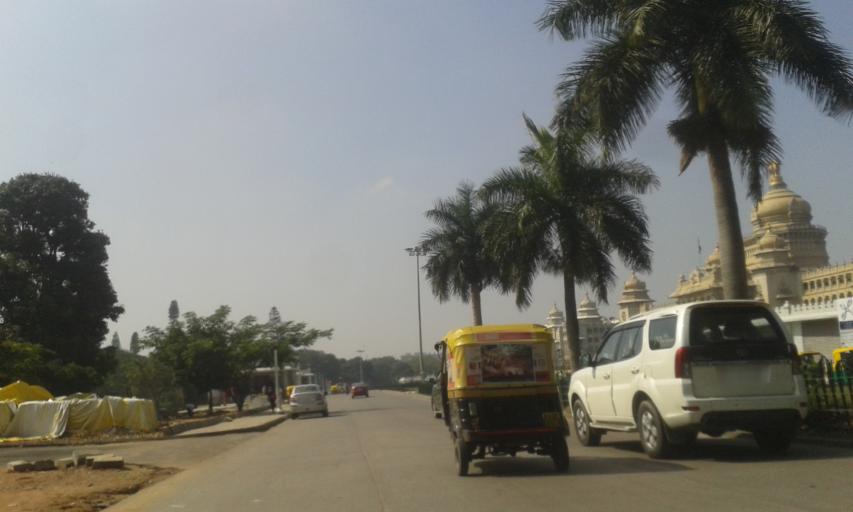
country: IN
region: Karnataka
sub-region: Bangalore Urban
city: Bangalore
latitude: 12.9802
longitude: 77.5932
